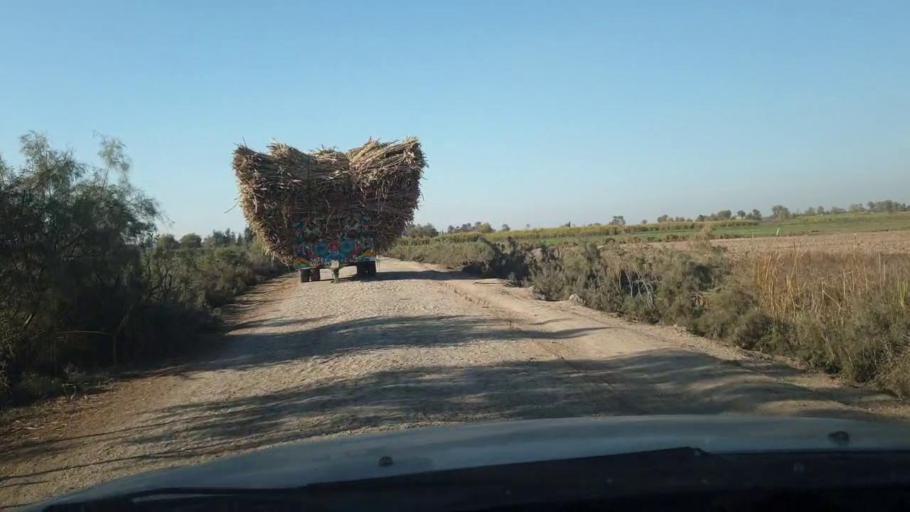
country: PK
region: Sindh
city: Ghotki
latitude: 28.0434
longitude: 69.2947
